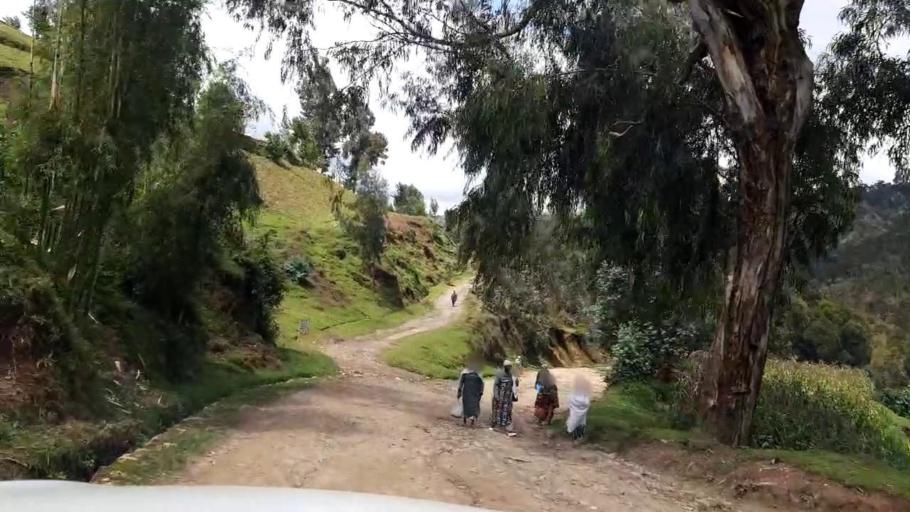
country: RW
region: Western Province
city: Kibuye
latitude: -1.9189
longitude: 29.4567
